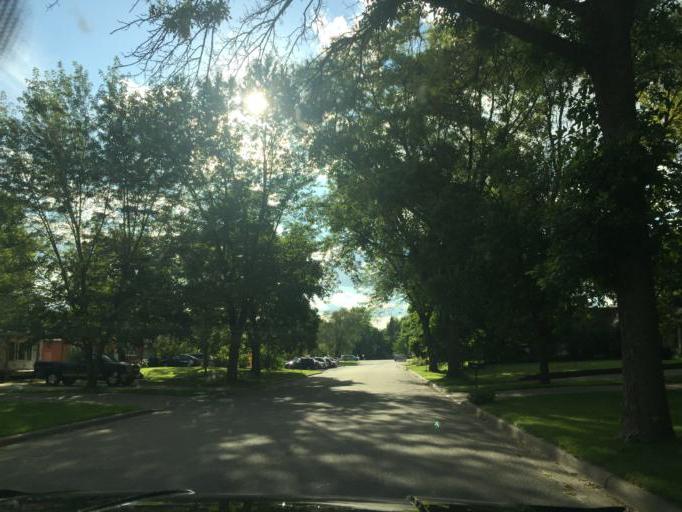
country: US
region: Minnesota
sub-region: Ramsey County
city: Roseville
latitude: 44.9950
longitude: -93.1442
